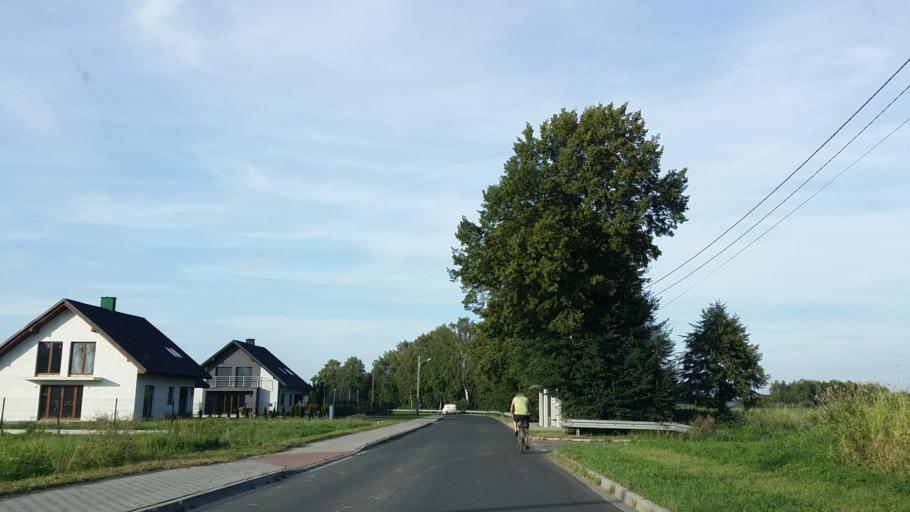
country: PL
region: Lesser Poland Voivodeship
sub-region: Powiat oswiecimski
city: Zator
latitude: 49.9891
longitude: 19.4195
